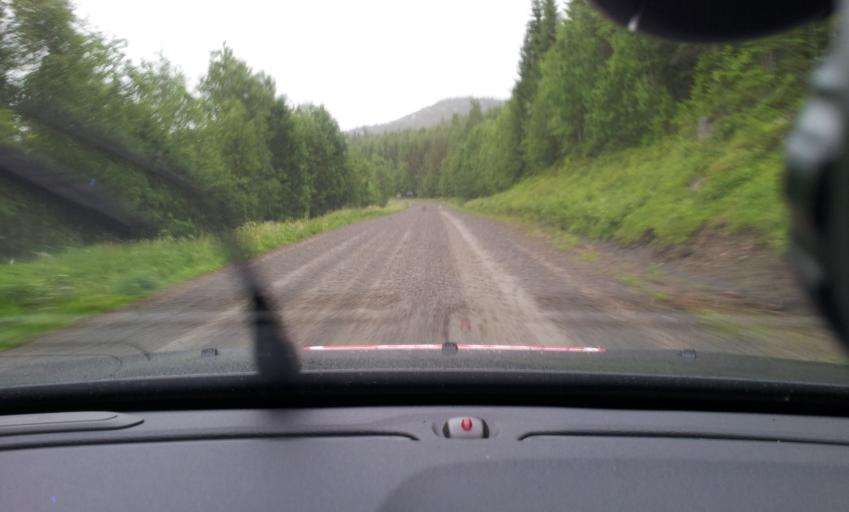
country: SE
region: Jaemtland
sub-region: Ragunda Kommun
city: Hammarstrand
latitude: 63.1343
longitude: 16.1136
